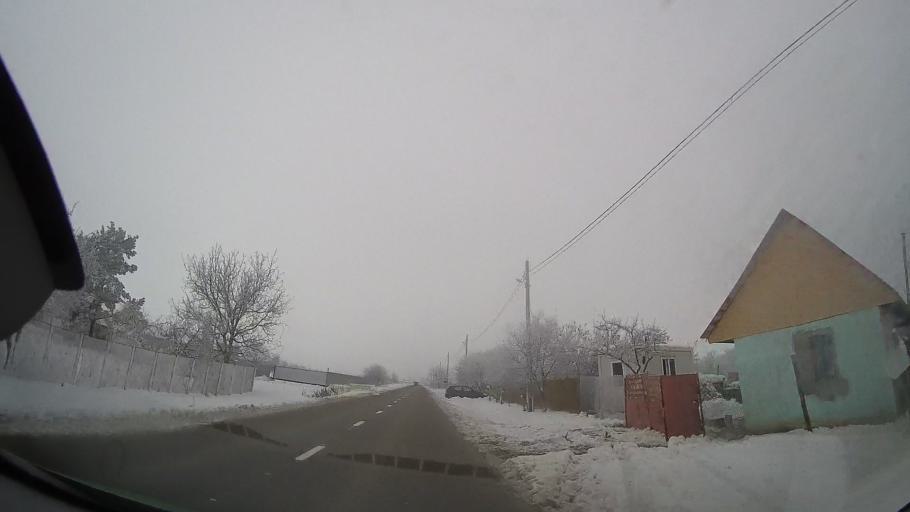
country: RO
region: Neamt
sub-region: Comuna Horia
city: Cotu Vames
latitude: 46.8889
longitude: 26.9665
